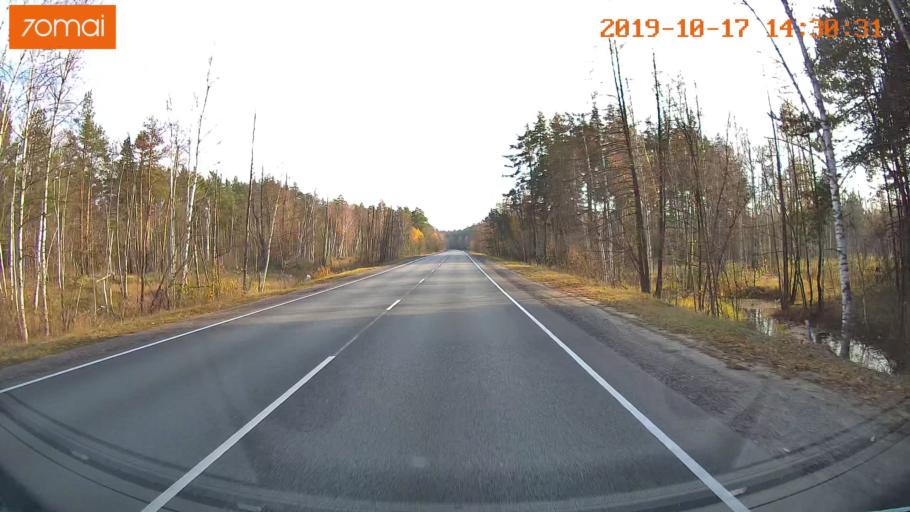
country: RU
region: Rjazan
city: Solotcha
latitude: 54.9467
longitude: 39.9471
